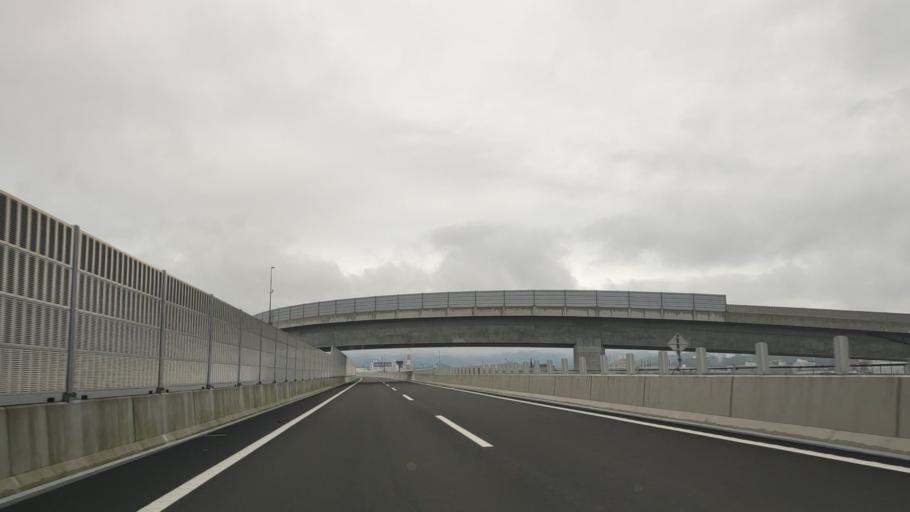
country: JP
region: Kanagawa
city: Atsugi
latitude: 35.4063
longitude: 139.3562
